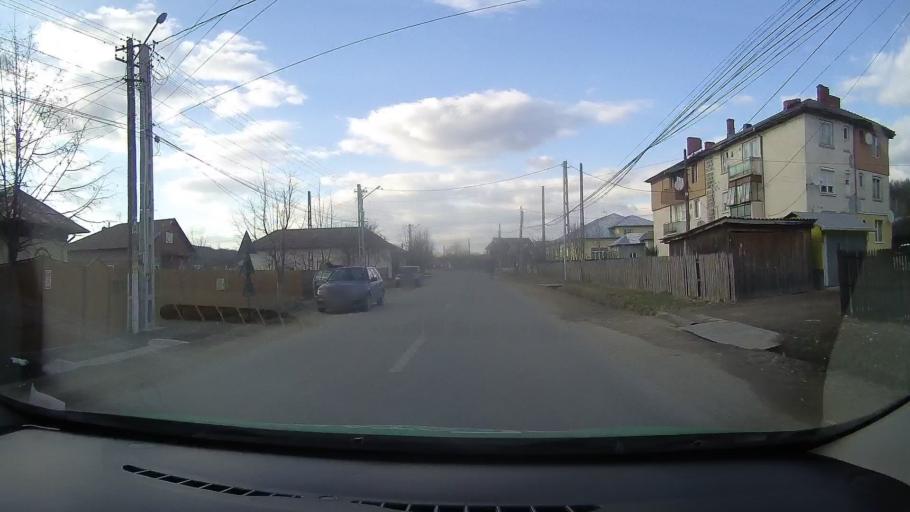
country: RO
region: Dambovita
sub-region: Comuna Gura Ocnitei
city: Gura Ocnitei
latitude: 44.9446
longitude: 25.5618
